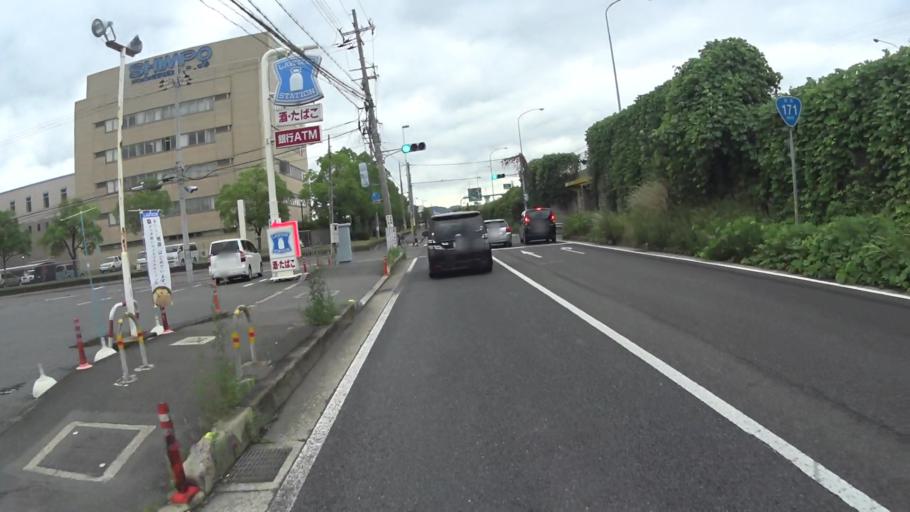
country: JP
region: Kyoto
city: Muko
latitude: 34.9246
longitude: 135.7116
